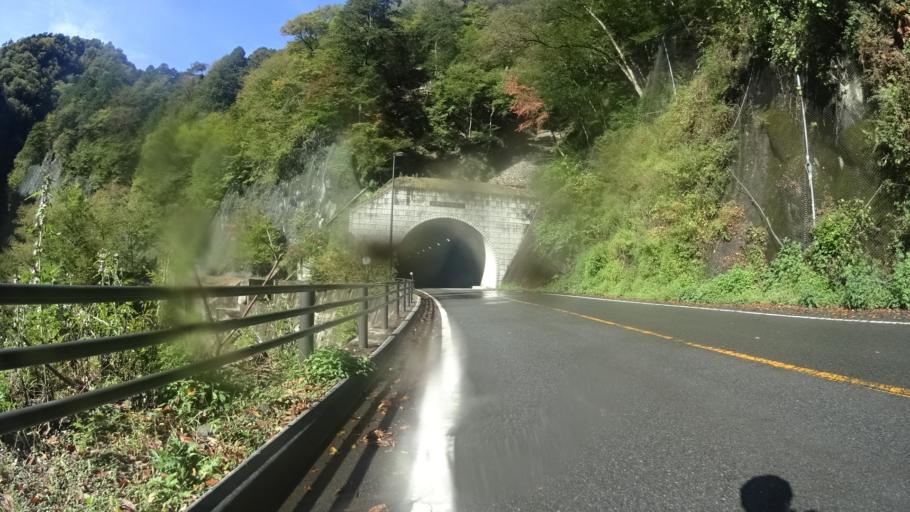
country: JP
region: Yamanashi
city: Enzan
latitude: 35.8065
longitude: 138.8630
